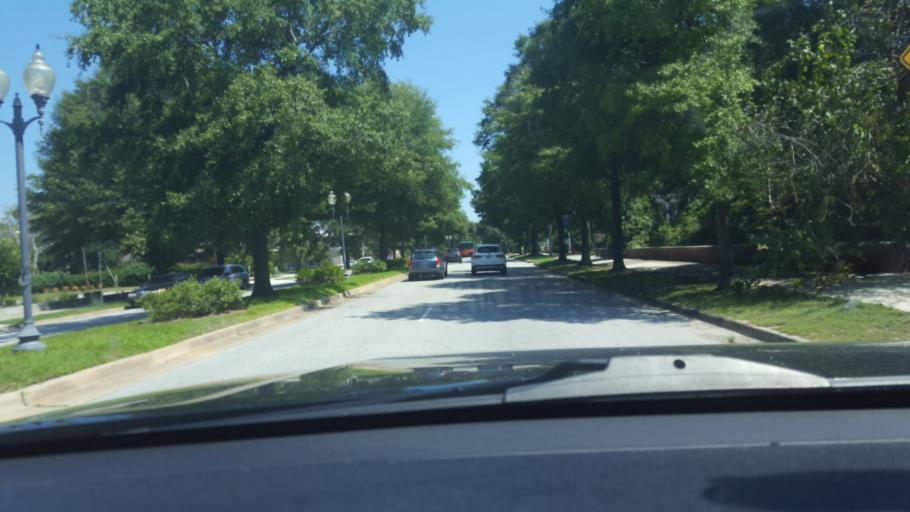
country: US
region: North Carolina
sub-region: New Hanover County
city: Wilmington
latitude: 34.2359
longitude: -77.9420
